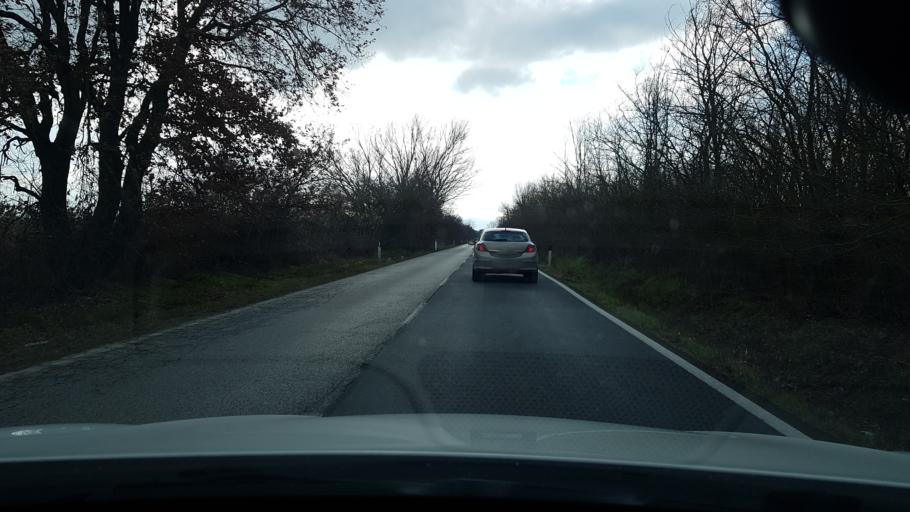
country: IT
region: Umbria
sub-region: Provincia di Perugia
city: Castiglione del Lago
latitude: 43.1374
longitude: 12.0262
